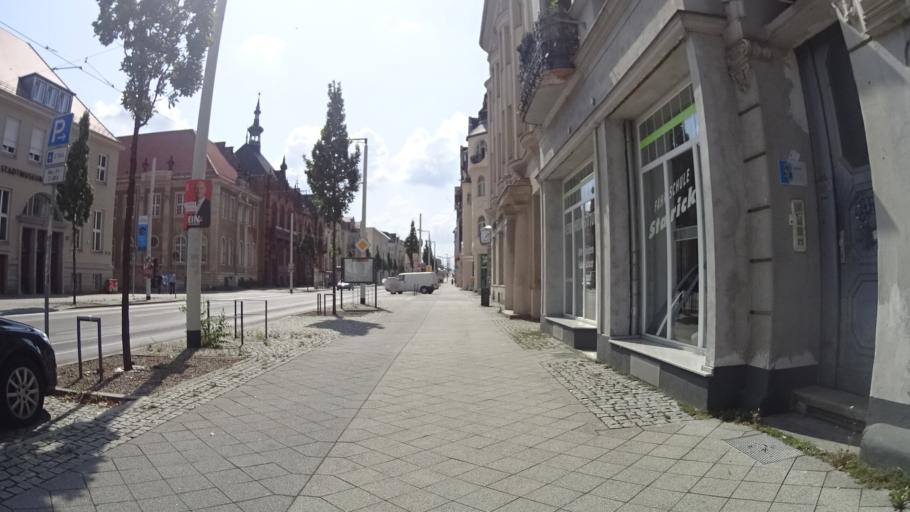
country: DE
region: Brandenburg
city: Cottbus
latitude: 51.7561
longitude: 14.3281
